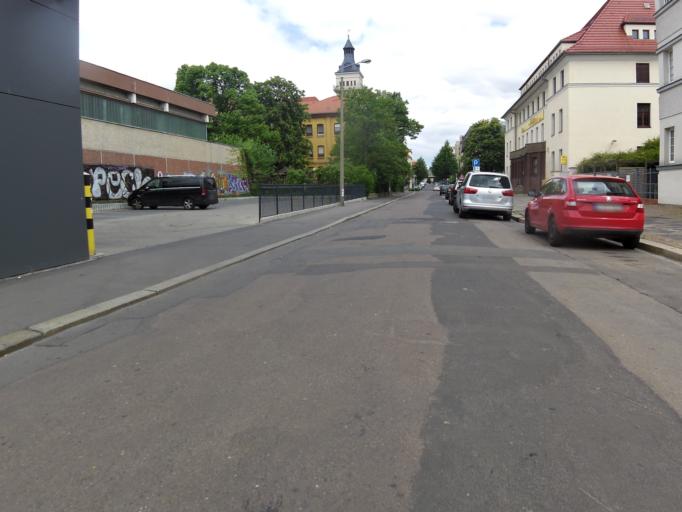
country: DE
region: Saxony
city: Leipzig
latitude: 51.3622
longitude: 12.3690
